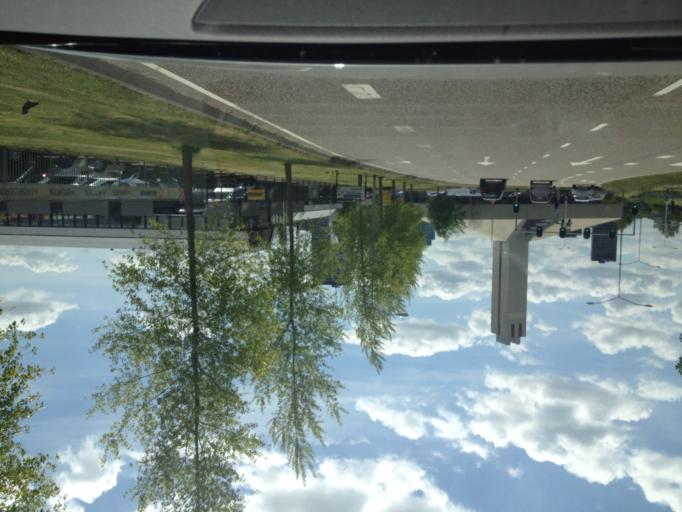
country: NL
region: Flevoland
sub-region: Gemeente Almere
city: Almere Stad
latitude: 52.3831
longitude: 5.2168
